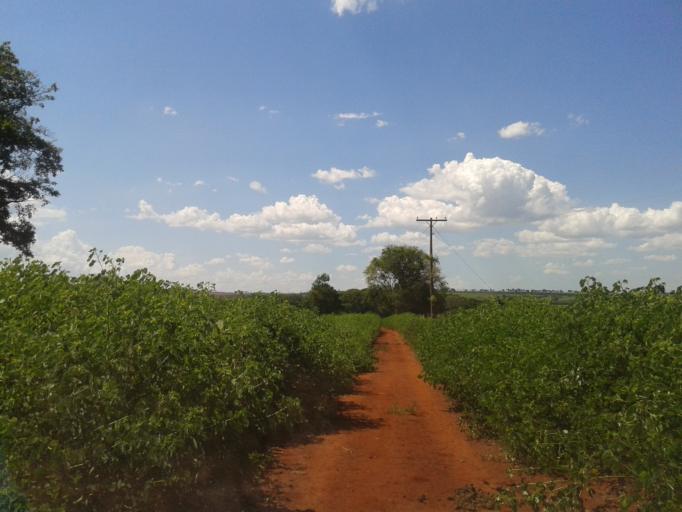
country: BR
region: Minas Gerais
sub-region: Santa Vitoria
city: Santa Vitoria
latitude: -19.1014
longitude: -50.5278
